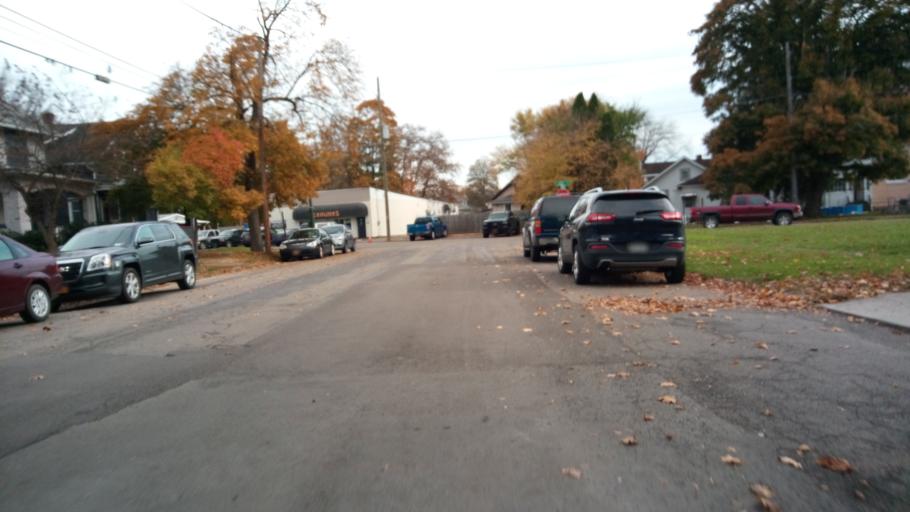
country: US
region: New York
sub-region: Chemung County
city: Elmira
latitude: 42.0802
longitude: -76.7897
